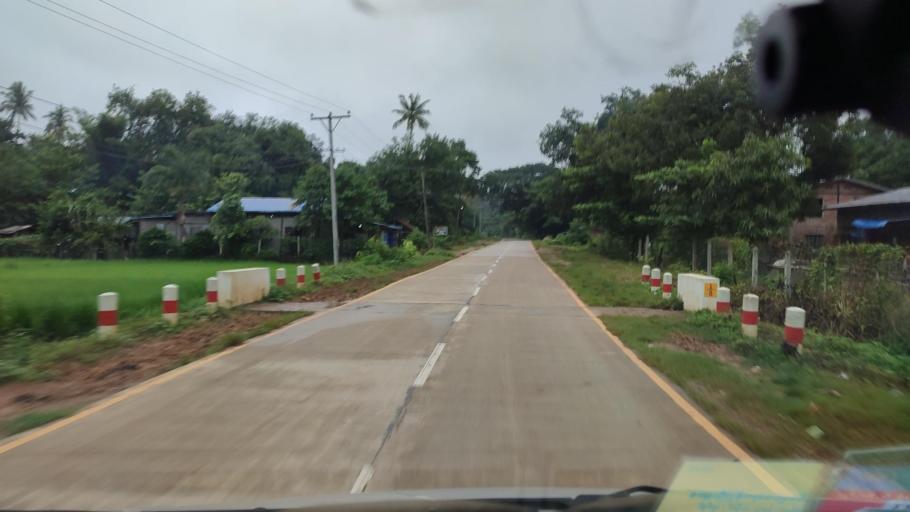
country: MM
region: Bago
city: Taungoo
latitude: 18.9930
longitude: 96.5213
